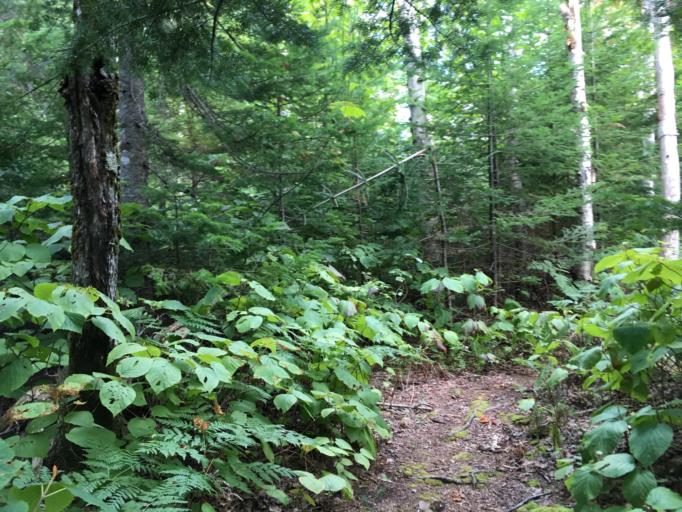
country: US
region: Maine
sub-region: Penobscot County
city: Millinocket
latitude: 45.9189
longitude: -68.8526
